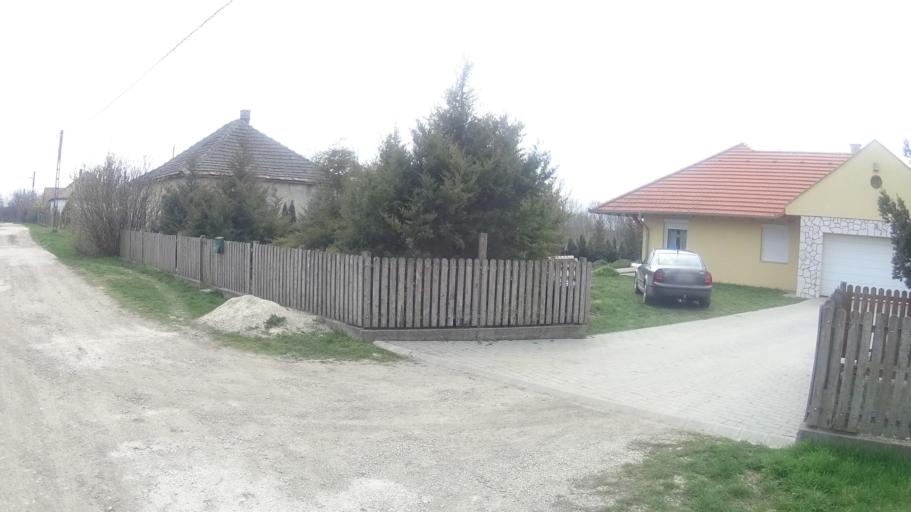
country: HU
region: Fejer
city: Sarosd
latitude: 46.9749
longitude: 18.6452
